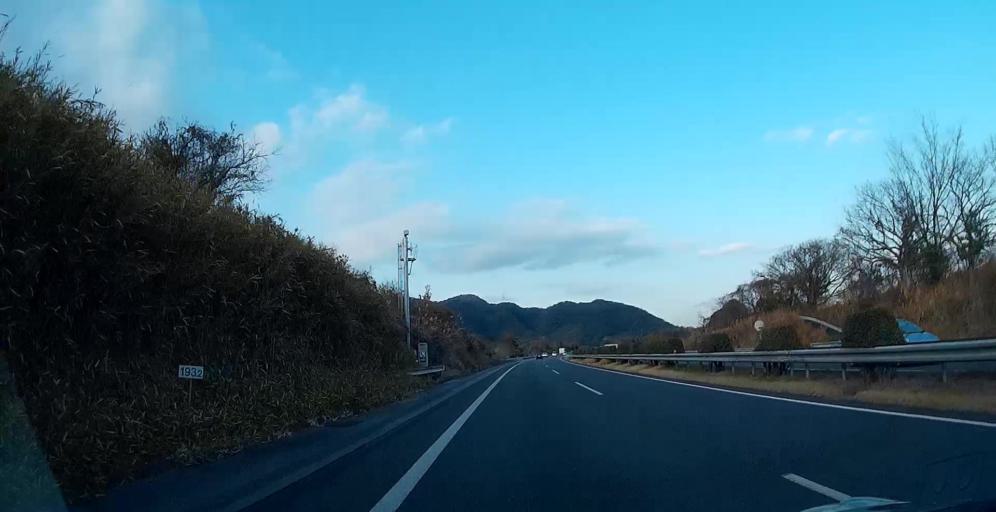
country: JP
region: Kumamoto
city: Matsubase
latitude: 32.6660
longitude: 130.7125
